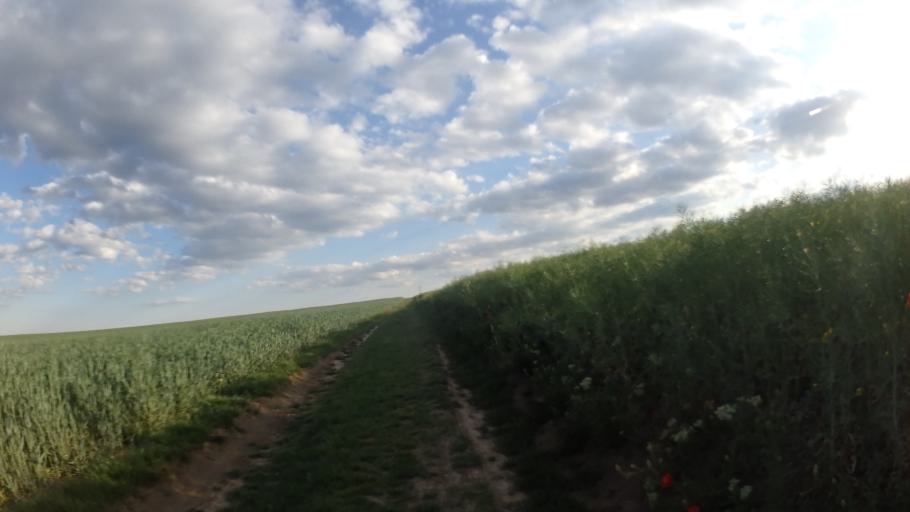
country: CZ
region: South Moravian
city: Moravany
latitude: 49.1398
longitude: 16.5919
